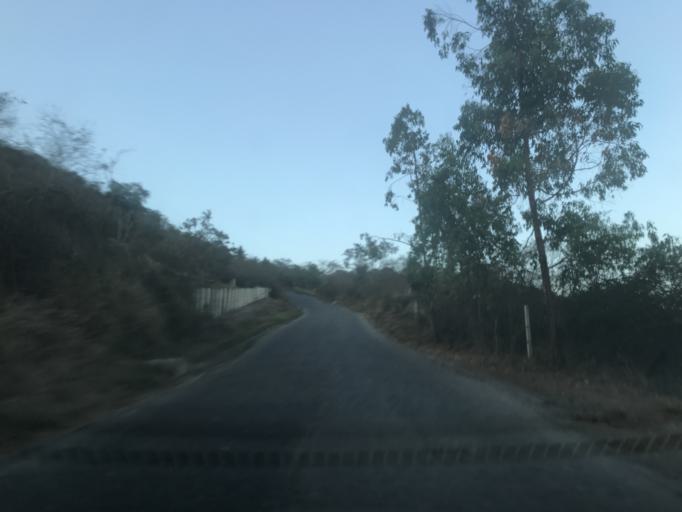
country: BR
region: Pernambuco
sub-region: Bezerros
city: Bezerros
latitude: -8.1860
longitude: -35.7616
